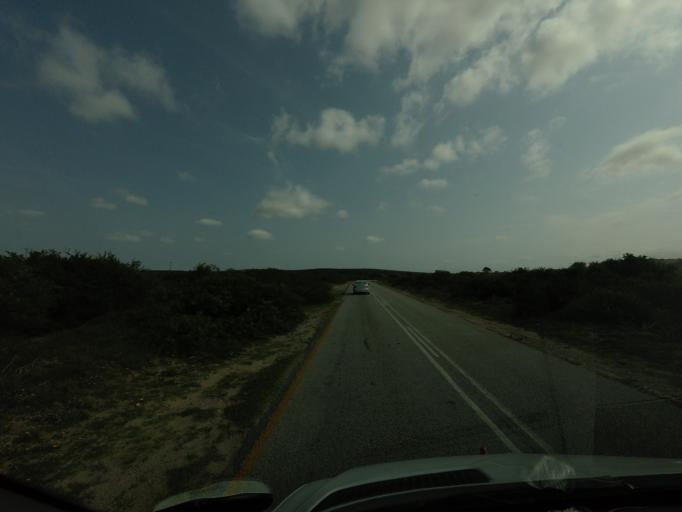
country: ZA
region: Eastern Cape
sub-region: Nelson Mandela Bay Metropolitan Municipality
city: Port Elizabeth
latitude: -33.7400
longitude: 25.5921
